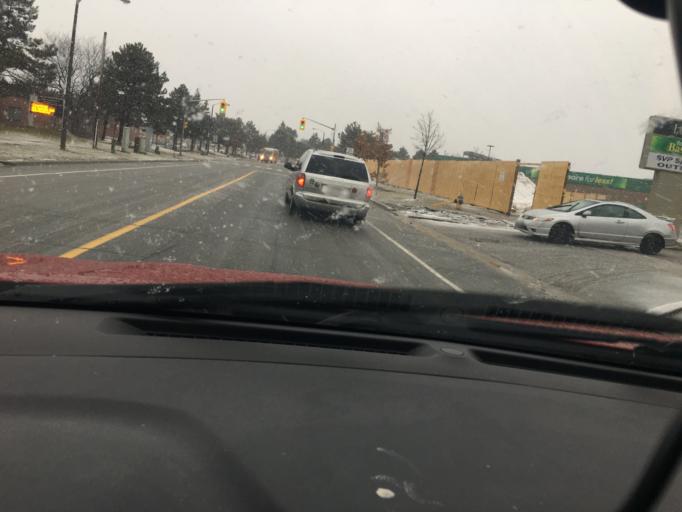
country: CA
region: Ontario
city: Scarborough
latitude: 43.8087
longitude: -79.2709
